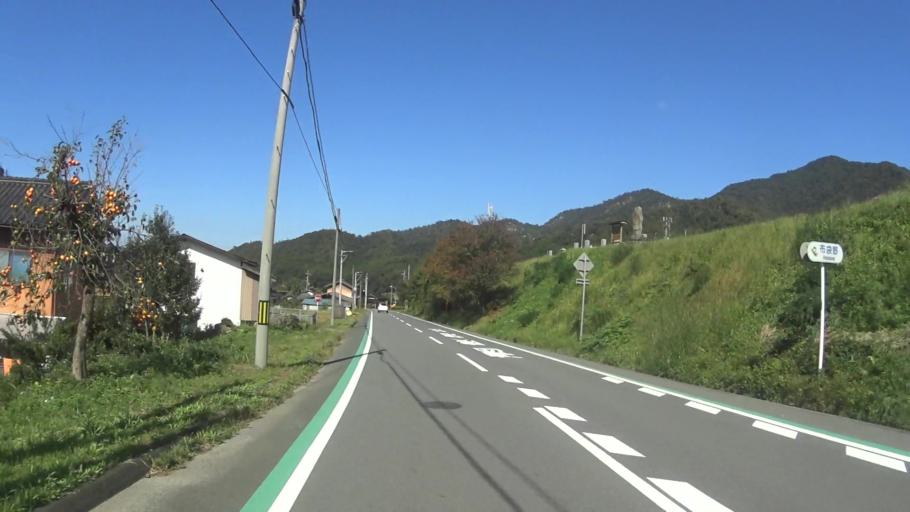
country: JP
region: Hyogo
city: Toyooka
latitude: 35.5419
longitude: 134.9406
